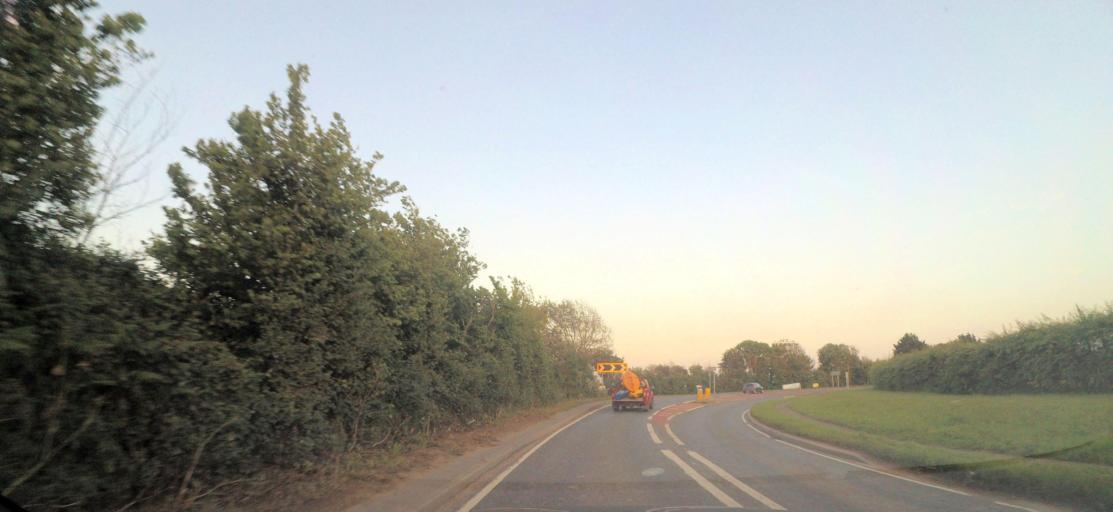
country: GB
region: England
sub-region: West Sussex
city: Selsey
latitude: 50.7463
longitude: -0.7796
